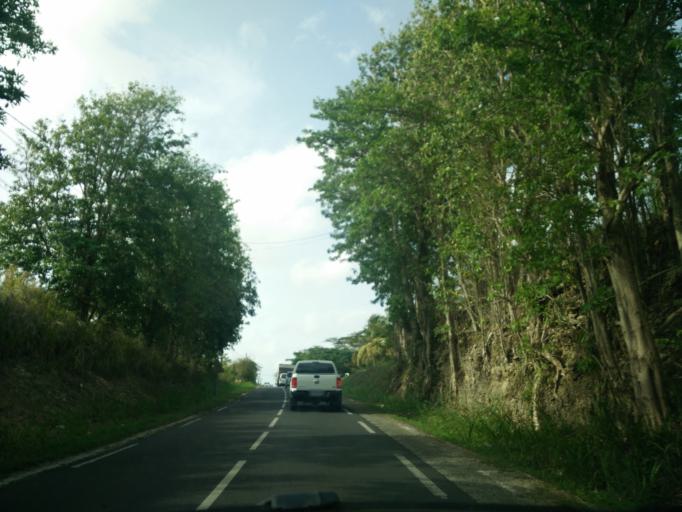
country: GP
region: Guadeloupe
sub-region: Guadeloupe
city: Sainte-Anne
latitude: 16.2765
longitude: -61.3761
